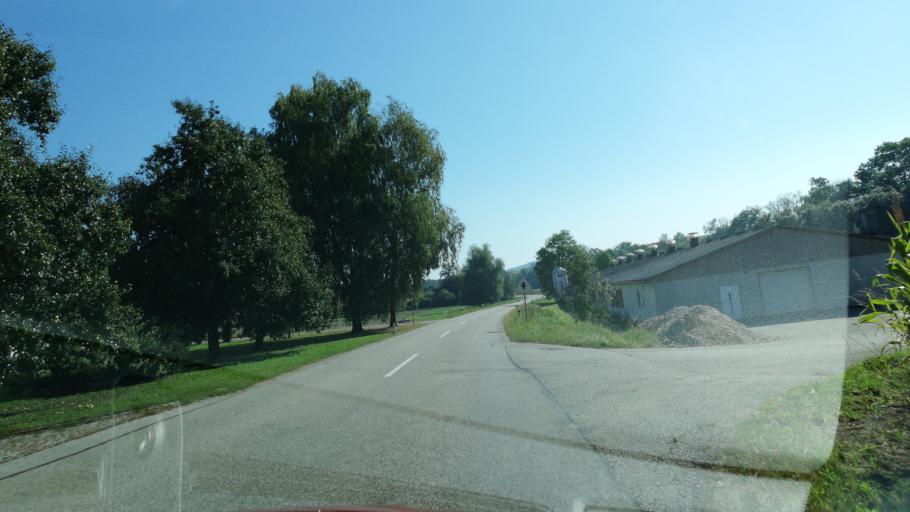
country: AT
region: Upper Austria
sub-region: Politischer Bezirk Grieskirchen
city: Bad Schallerbach
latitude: 48.1959
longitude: 13.8949
